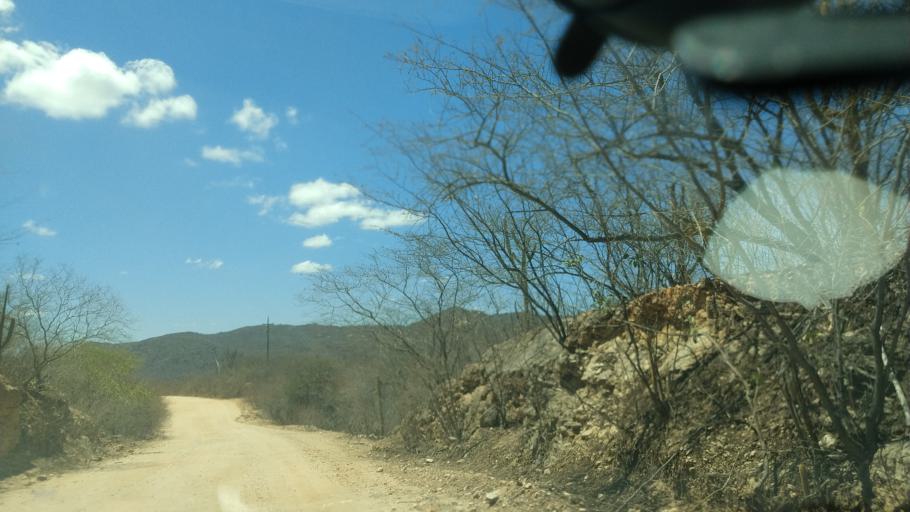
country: BR
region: Rio Grande do Norte
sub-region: Cerro Cora
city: Cerro Cora
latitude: -6.0145
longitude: -36.3043
